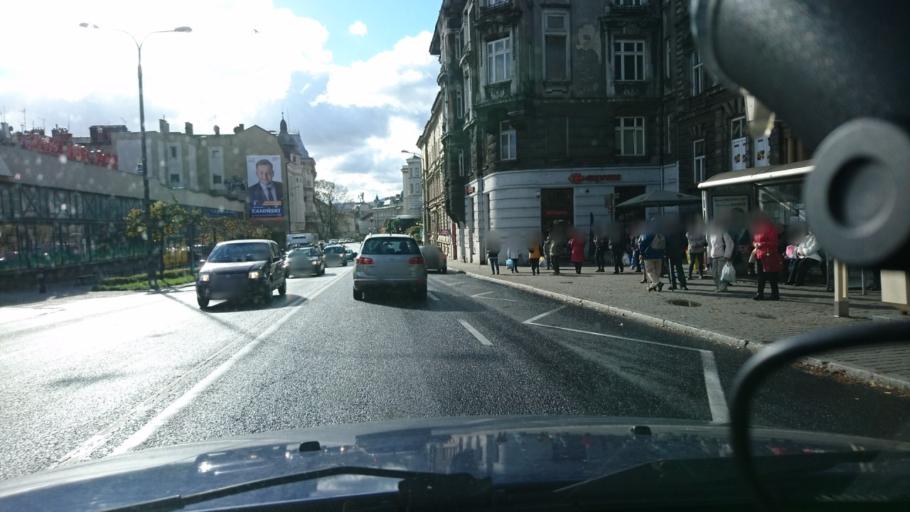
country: PL
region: Silesian Voivodeship
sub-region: Bielsko-Biala
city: Bielsko-Biala
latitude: 49.8235
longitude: 19.0449
